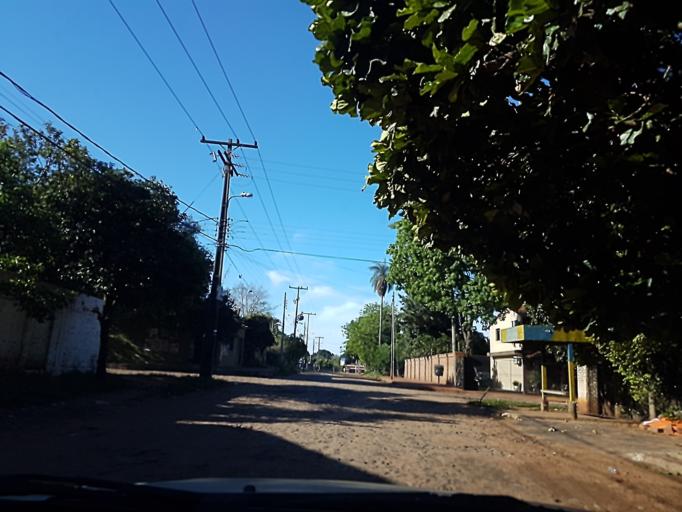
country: PY
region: Central
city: San Lorenzo
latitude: -25.2768
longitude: -57.4644
